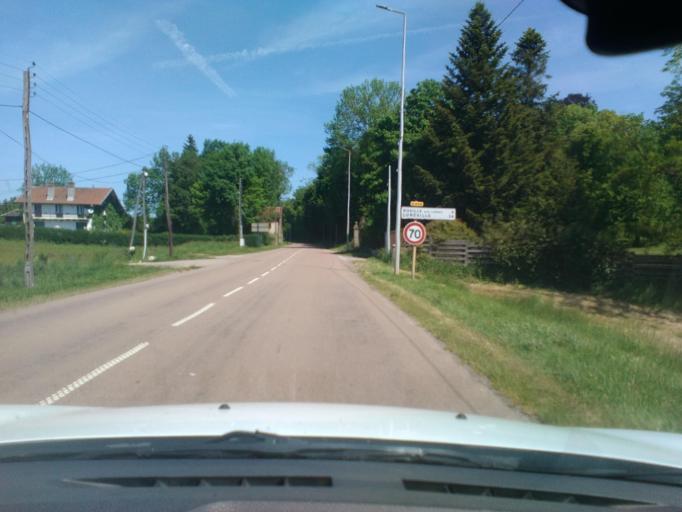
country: FR
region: Lorraine
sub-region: Departement des Vosges
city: Rambervillers
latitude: 48.3545
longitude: 6.6309
